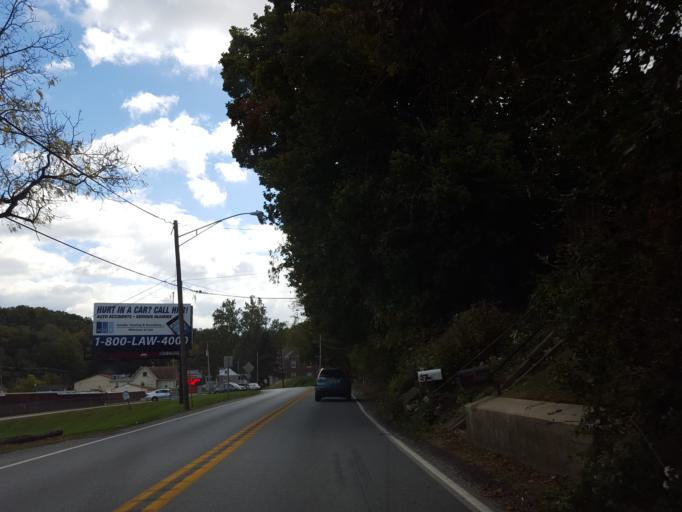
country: US
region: Pennsylvania
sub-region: York County
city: Grantley
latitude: 39.9392
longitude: -76.7170
